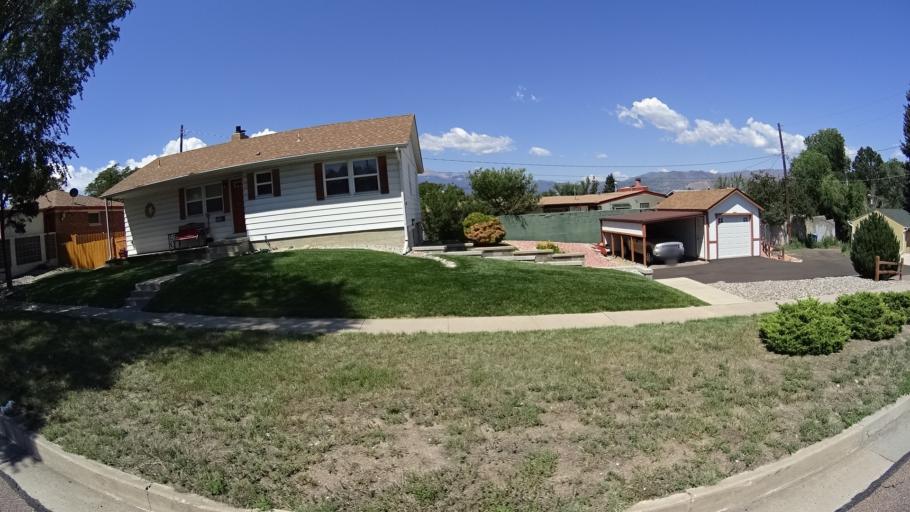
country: US
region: Colorado
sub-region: El Paso County
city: Colorado Springs
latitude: 38.8513
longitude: -104.7943
